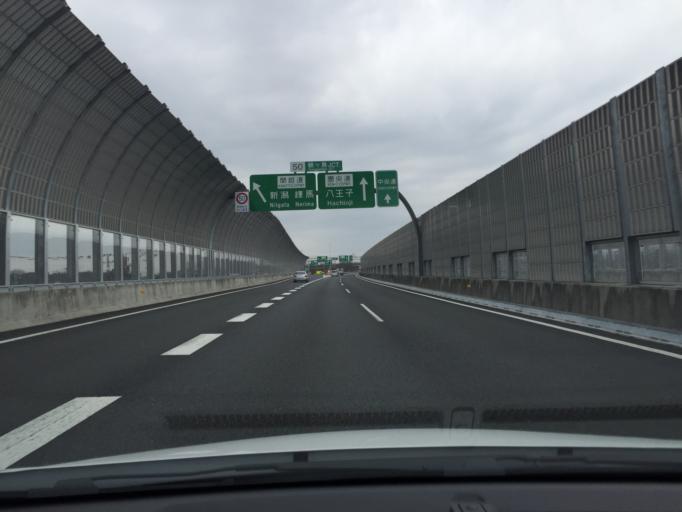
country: JP
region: Saitama
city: Sakado
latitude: 35.9362
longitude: 139.4074
